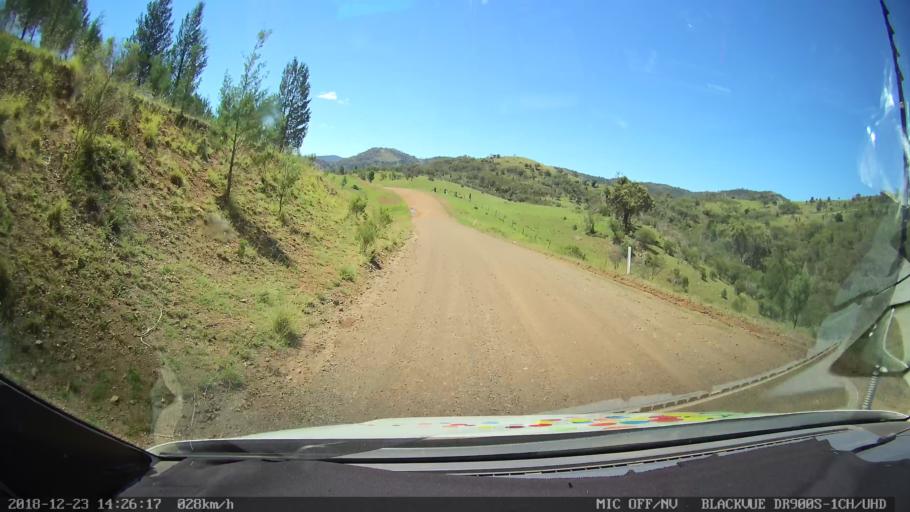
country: AU
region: New South Wales
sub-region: Tamworth Municipality
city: Manilla
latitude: -30.6236
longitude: 150.9534
